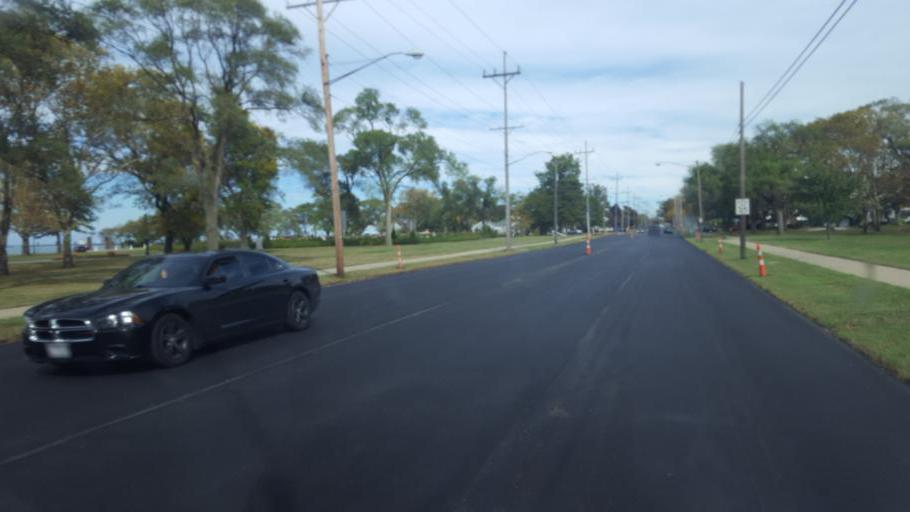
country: US
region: Ohio
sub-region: Lorain County
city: Lorain
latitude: 41.4622
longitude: -82.1950
